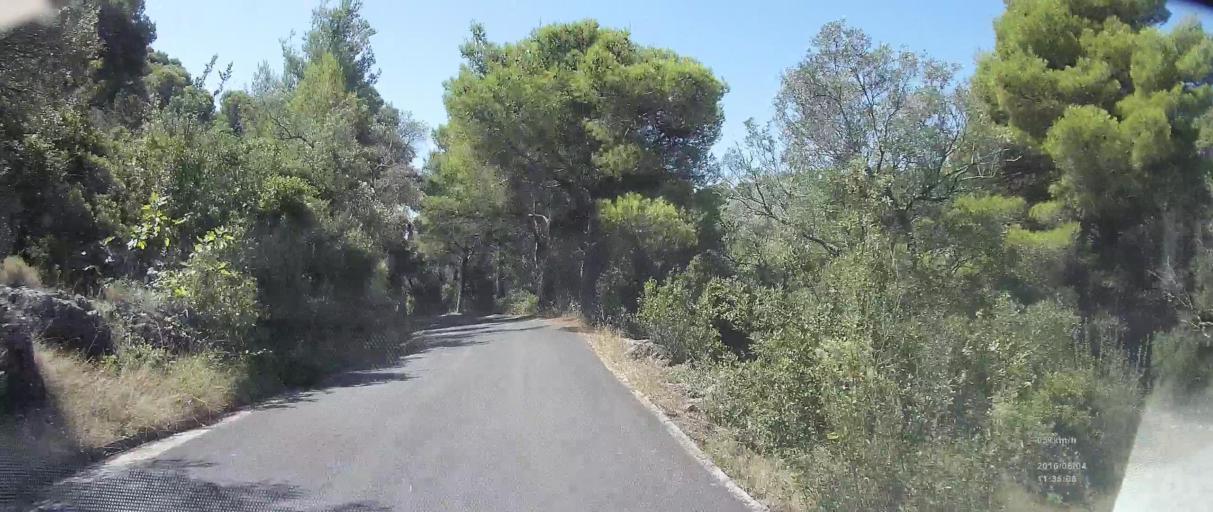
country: HR
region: Dubrovacko-Neretvanska
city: Blato
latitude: 42.7816
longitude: 17.3668
